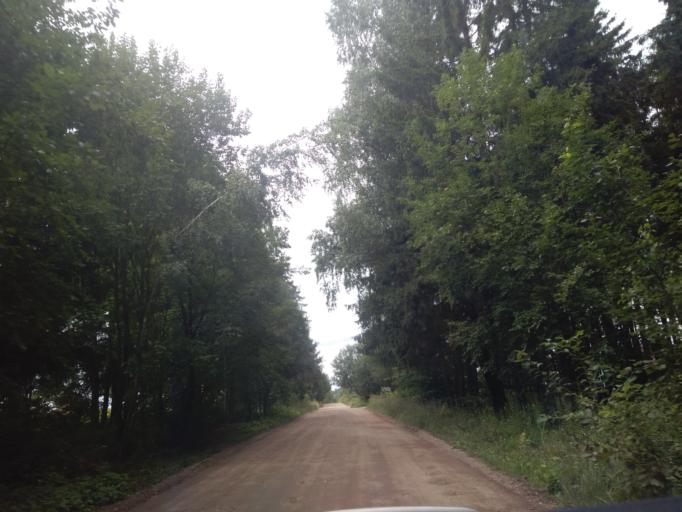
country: BY
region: Minsk
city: Slabada
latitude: 53.9858
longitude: 27.9081
